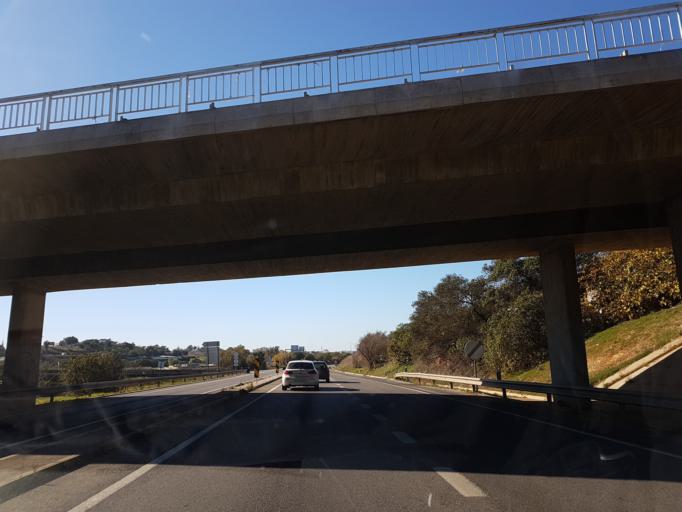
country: PT
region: Faro
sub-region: Lagoa
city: Estombar
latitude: 37.1520
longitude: -8.4954
